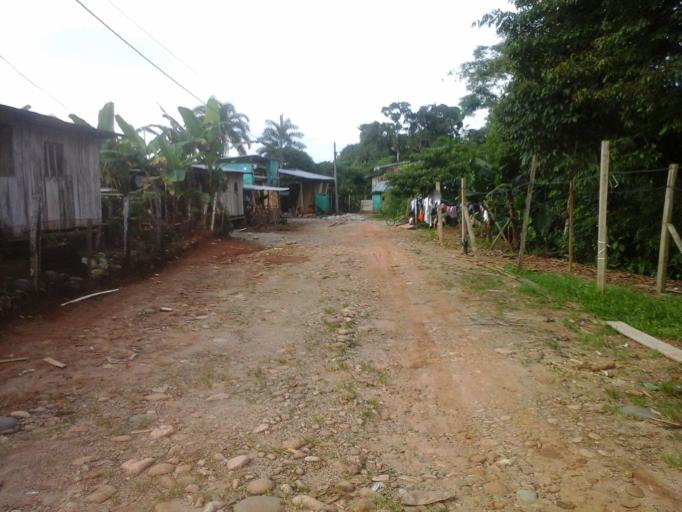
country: CO
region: Putumayo
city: Orito
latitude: 0.6496
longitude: -76.8236
